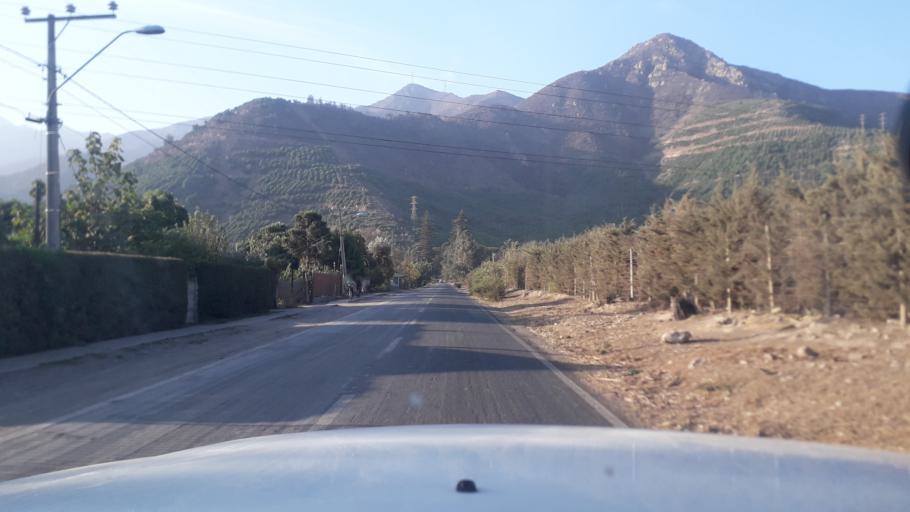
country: CL
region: Valparaiso
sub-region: Provincia de San Felipe
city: Llaillay
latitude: -32.8232
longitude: -71.0288
